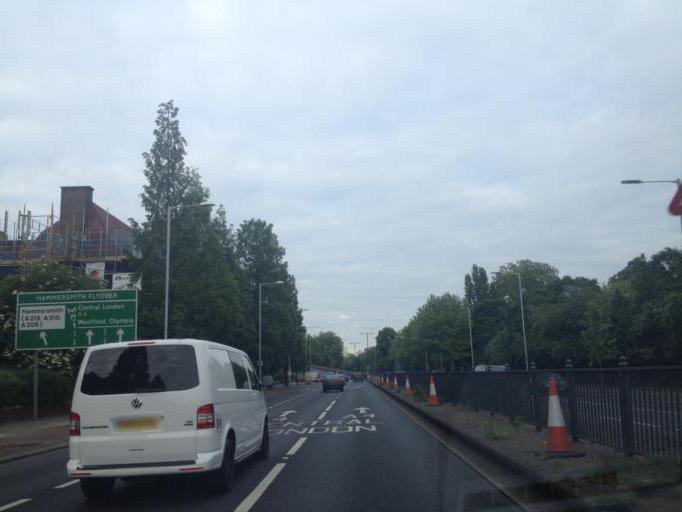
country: GB
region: England
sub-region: Greater London
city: Hammersmith
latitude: 51.4913
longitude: -0.2339
